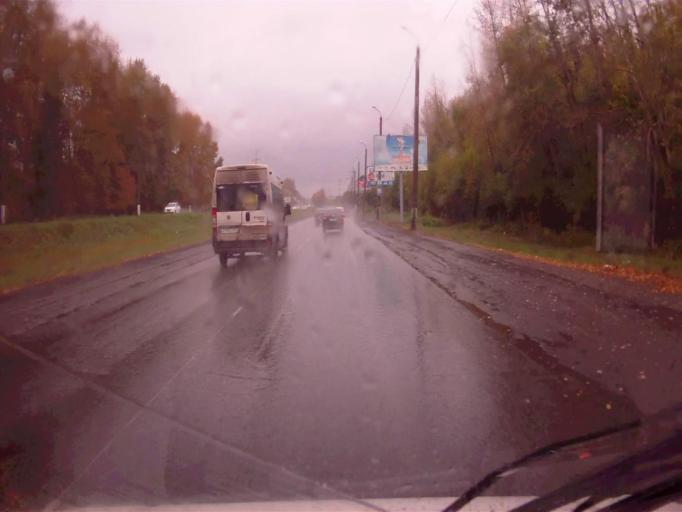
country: RU
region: Chelyabinsk
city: Dolgoderevenskoye
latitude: 55.2440
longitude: 61.3601
